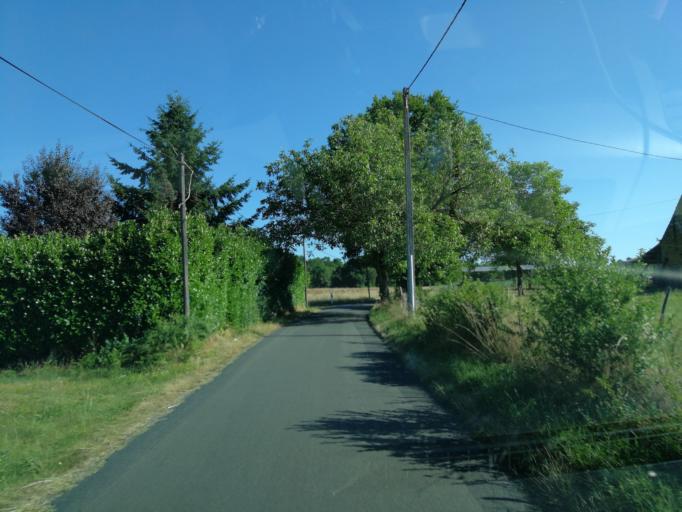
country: FR
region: Midi-Pyrenees
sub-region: Departement du Lot
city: Gourdon
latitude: 44.8248
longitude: 1.3602
